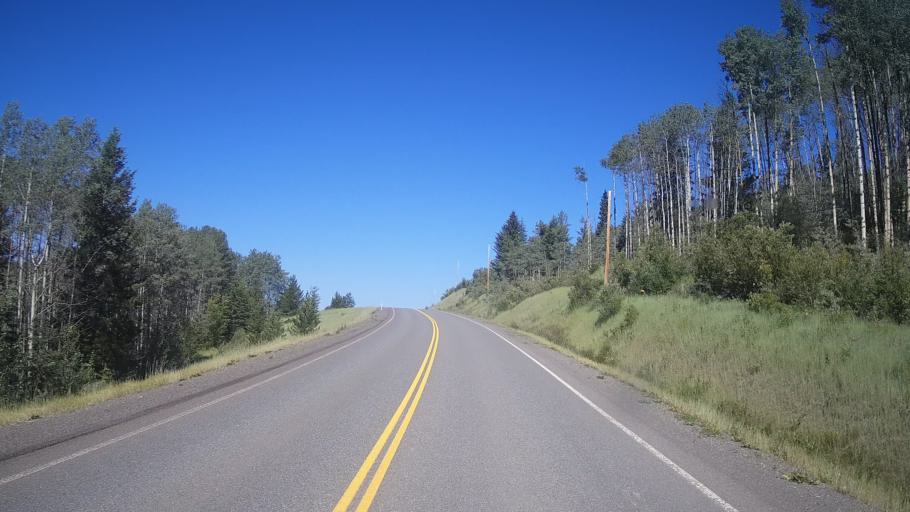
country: CA
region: British Columbia
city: Kamloops
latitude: 51.4958
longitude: -120.5779
